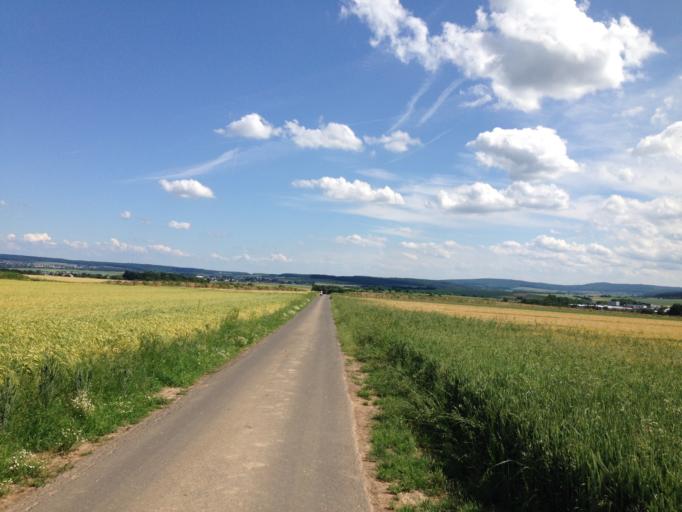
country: DE
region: Hesse
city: Allendorf an der Lahn
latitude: 50.5340
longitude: 8.5920
